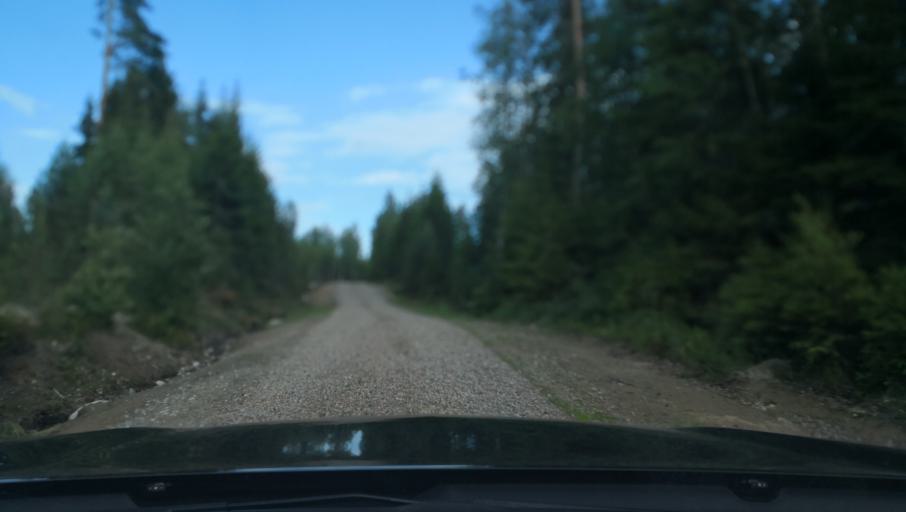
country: SE
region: Dalarna
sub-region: Smedjebackens Kommun
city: Smedjebacken
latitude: 60.0700
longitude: 15.2987
